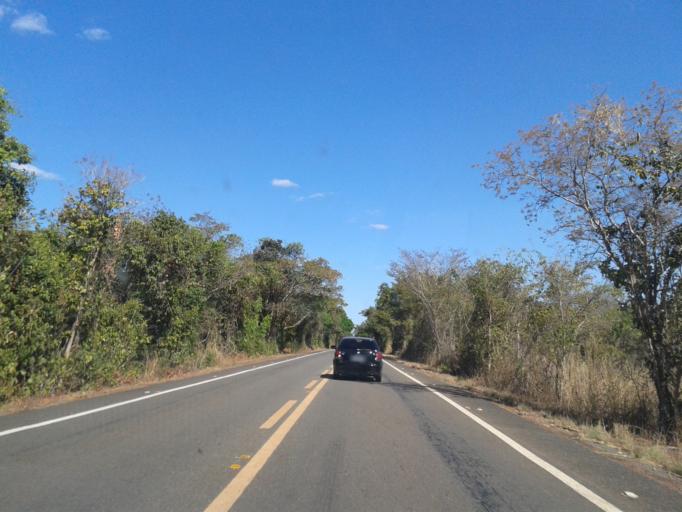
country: BR
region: Goias
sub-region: Sao Miguel Do Araguaia
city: Sao Miguel do Araguaia
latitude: -13.8680
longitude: -50.3329
